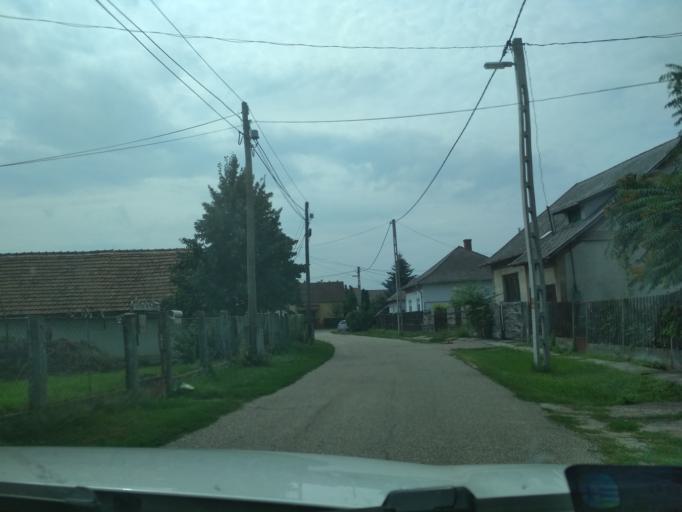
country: HU
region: Jasz-Nagykun-Szolnok
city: Tiszafured
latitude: 47.6148
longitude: 20.7536
